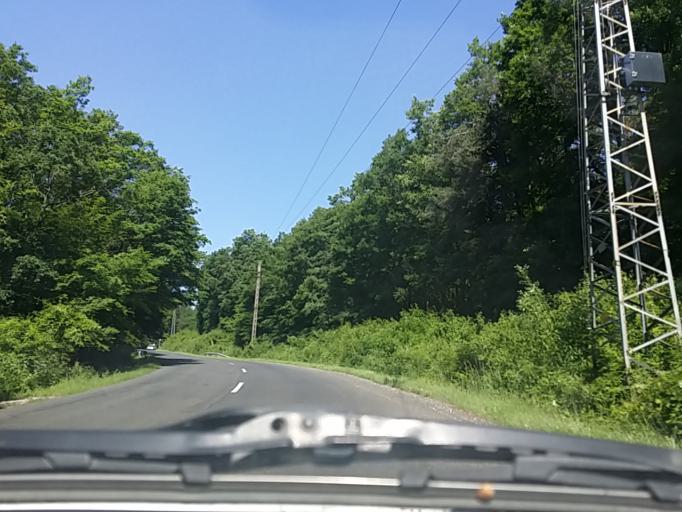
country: HU
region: Pest
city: Pilisszentkereszt
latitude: 47.7030
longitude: 18.8900
